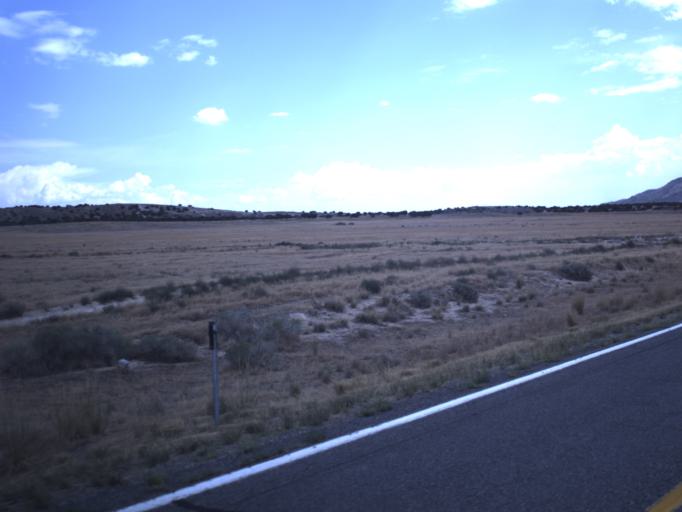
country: US
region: Utah
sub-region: Utah County
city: Eagle Mountain
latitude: 40.2463
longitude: -112.2125
